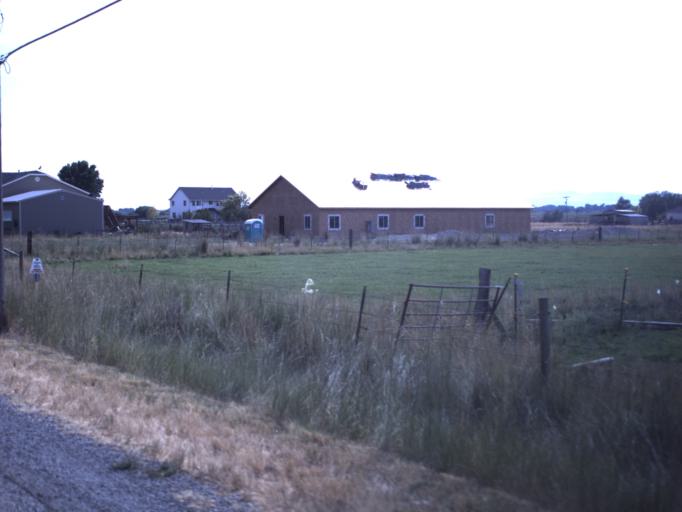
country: US
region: Utah
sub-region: Box Elder County
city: Elwood
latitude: 41.6969
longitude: -112.0901
